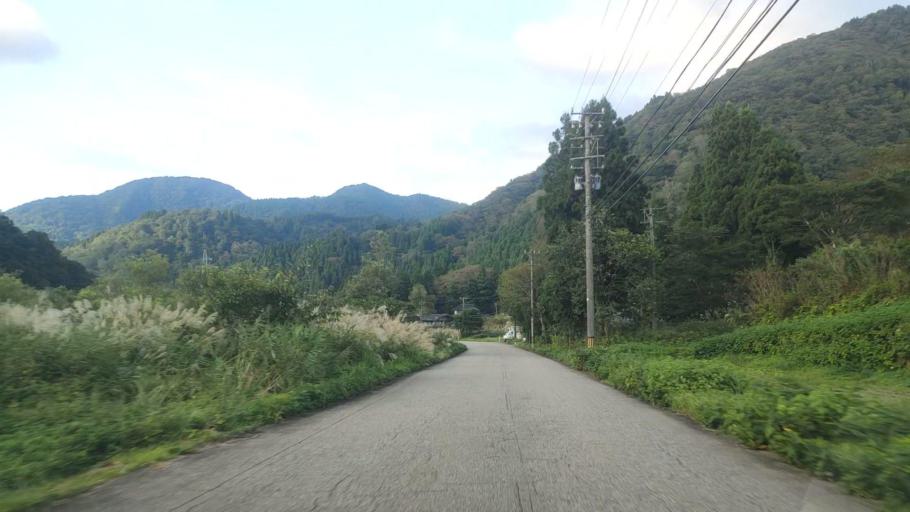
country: JP
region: Toyama
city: Yatsuomachi-higashikumisaka
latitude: 36.4732
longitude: 137.0853
